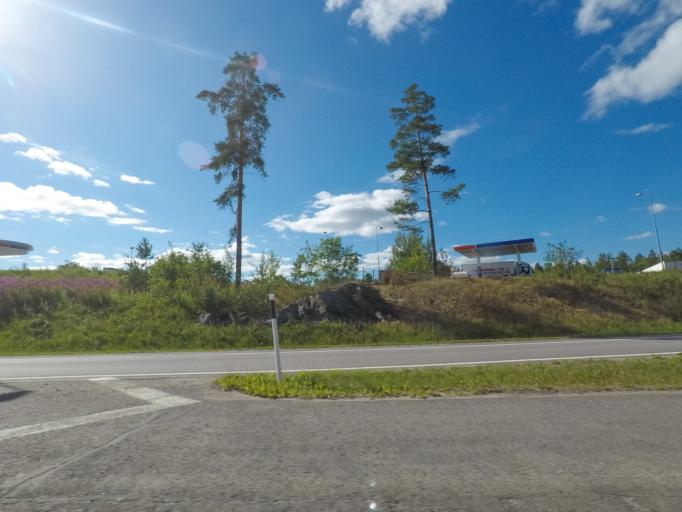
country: FI
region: Paijanne Tavastia
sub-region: Lahti
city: Heinola
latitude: 61.2189
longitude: 26.0150
